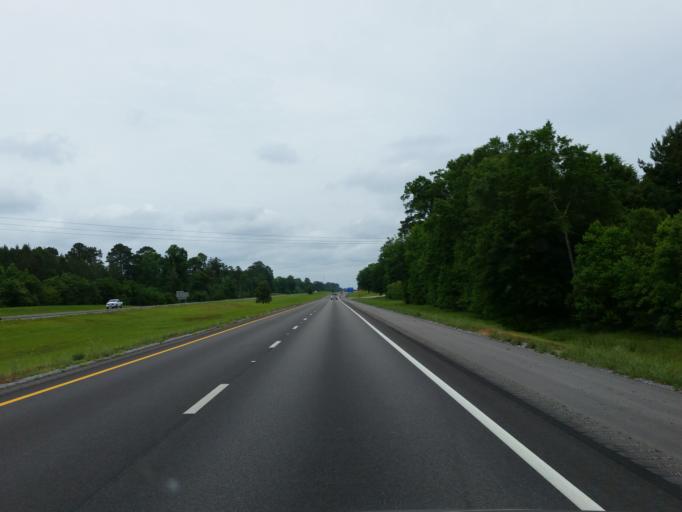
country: US
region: Mississippi
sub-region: Jones County
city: Sharon
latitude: 31.7994
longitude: -89.0539
